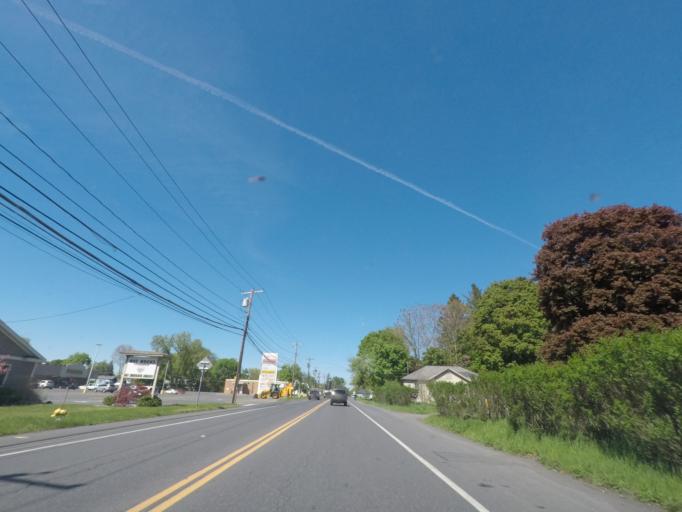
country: US
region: New York
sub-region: Ulster County
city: Saugerties South
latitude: 42.0570
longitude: -73.9549
